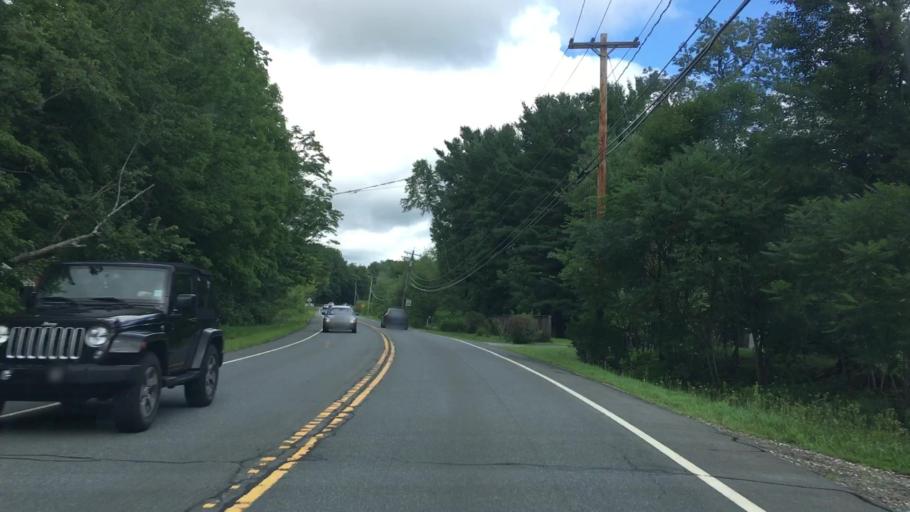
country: US
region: New York
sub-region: Rensselaer County
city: Poestenkill
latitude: 42.8256
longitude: -73.4960
